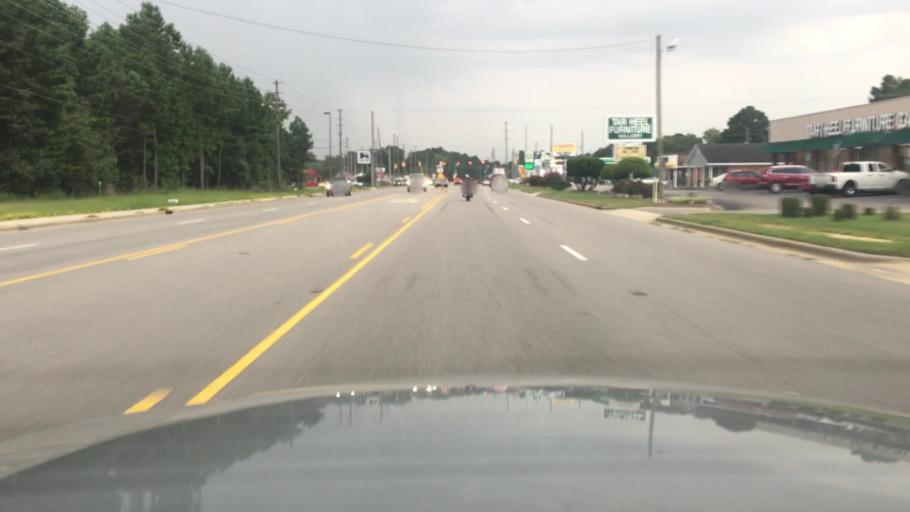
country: US
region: North Carolina
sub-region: Cumberland County
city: Fort Bragg
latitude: 35.0849
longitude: -79.0104
